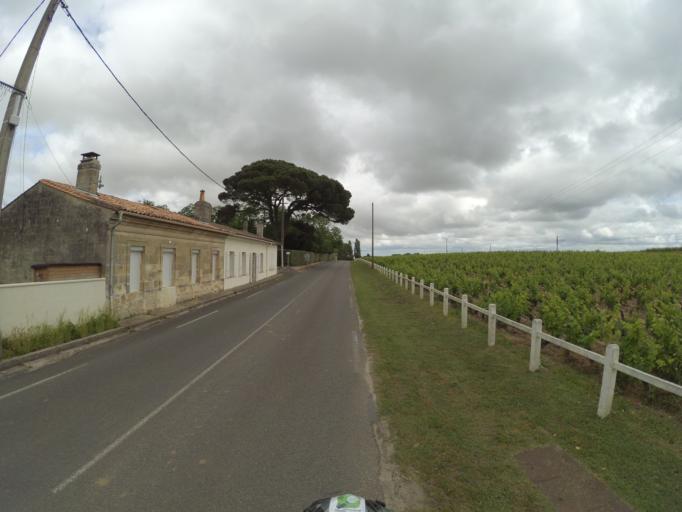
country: FR
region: Aquitaine
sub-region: Departement de la Gironde
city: Cantenac
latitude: 45.0223
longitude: -0.6366
